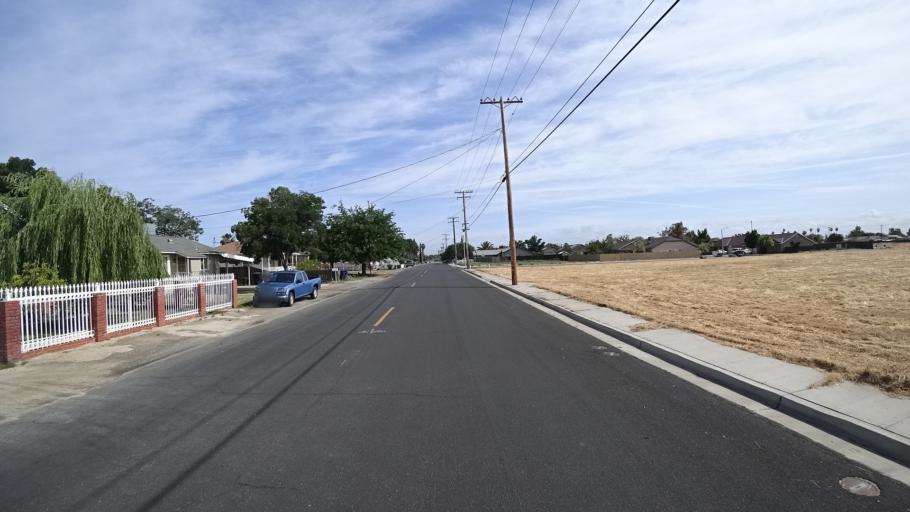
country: US
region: California
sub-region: Kings County
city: Hanford
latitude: 36.3149
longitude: -119.6616
